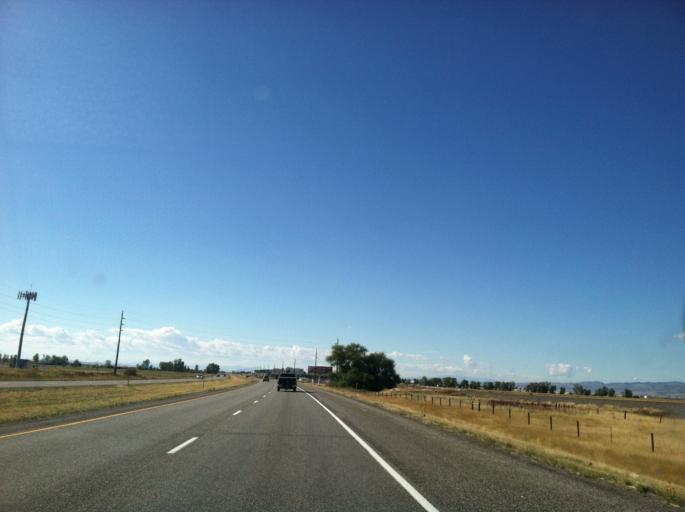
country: US
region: Montana
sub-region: Gallatin County
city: Belgrade
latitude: 45.7460
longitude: -111.1217
